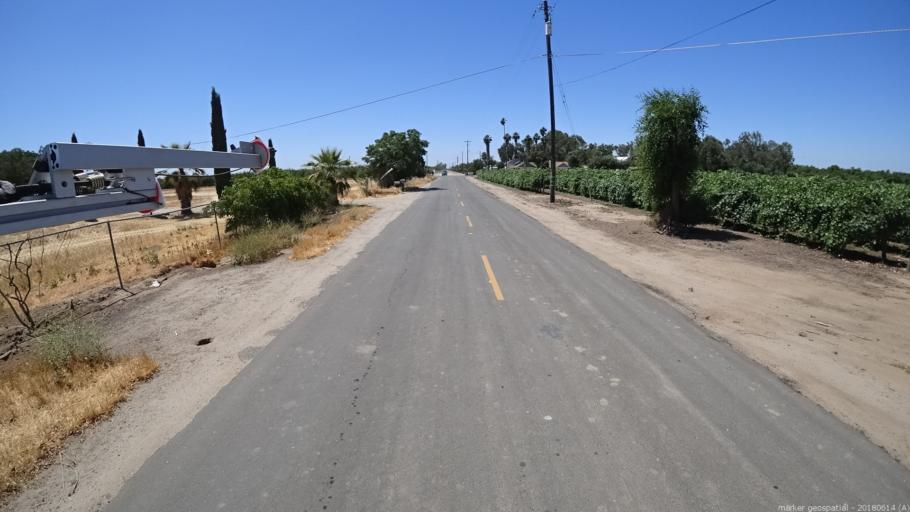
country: US
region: California
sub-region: Madera County
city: Fairmead
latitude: 37.0193
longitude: -120.2387
